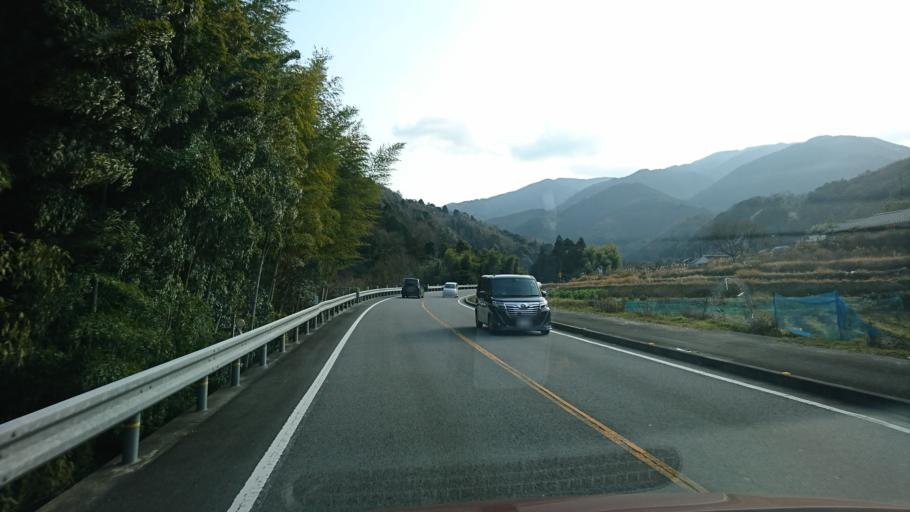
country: JP
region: Ehime
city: Hojo
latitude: 33.9789
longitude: 132.9049
